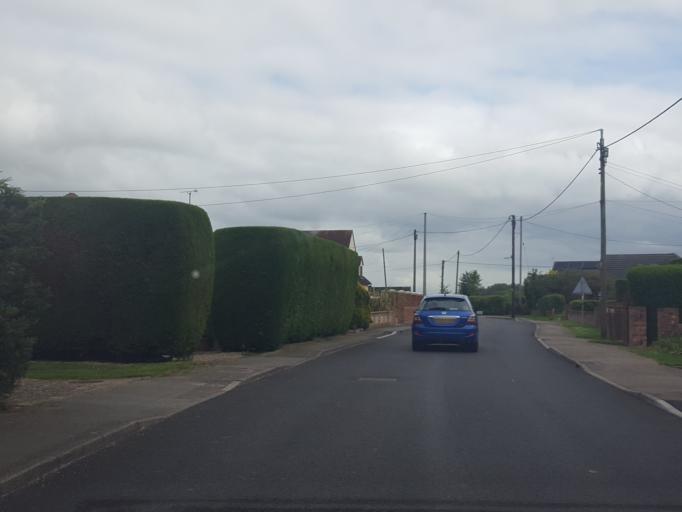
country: GB
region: England
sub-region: Essex
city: Little Clacton
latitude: 51.8433
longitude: 1.1233
